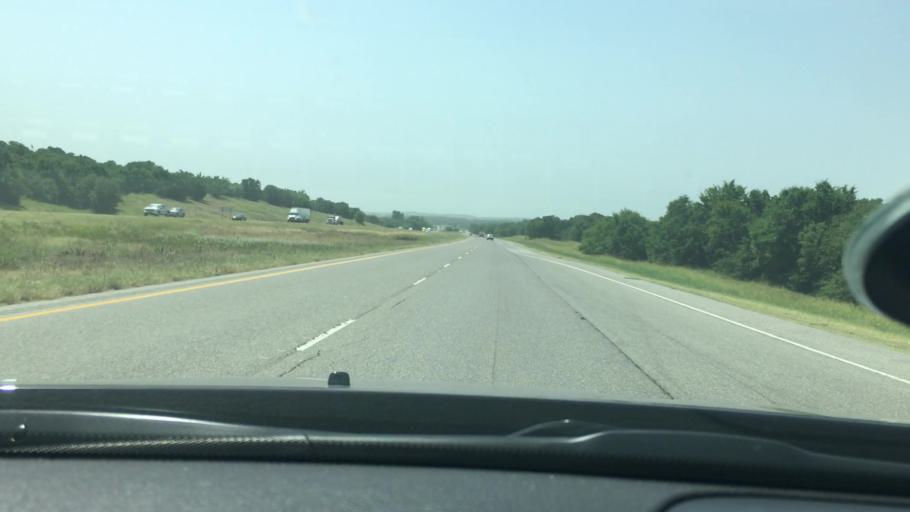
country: US
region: Oklahoma
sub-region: Murray County
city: Davis
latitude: 34.5440
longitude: -97.1902
